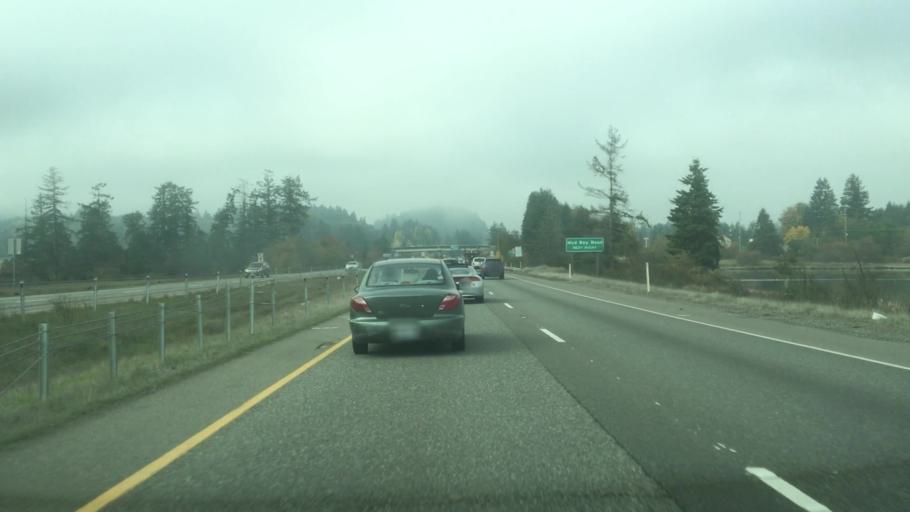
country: US
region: Washington
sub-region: Thurston County
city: Tumwater
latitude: 47.0440
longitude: -122.9888
